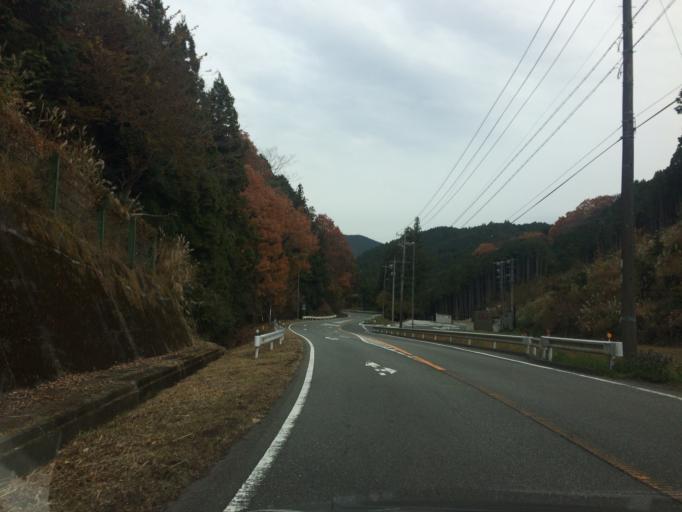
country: JP
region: Shizuoka
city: Fujinomiya
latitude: 35.1838
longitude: 138.5280
